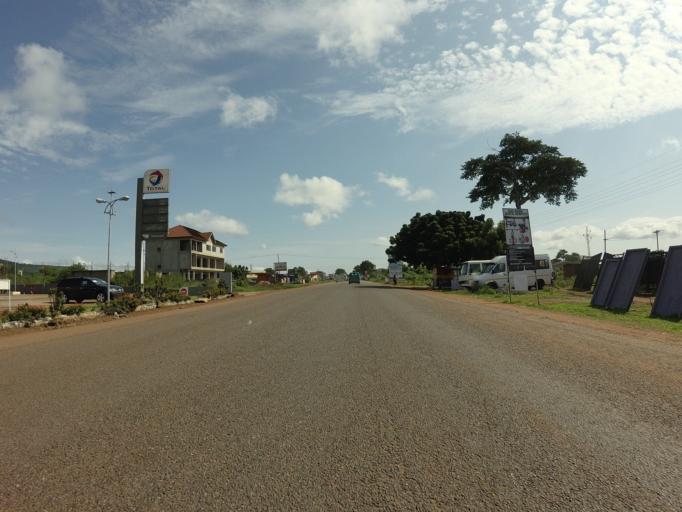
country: GH
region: Eastern
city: Aburi
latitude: 5.7942
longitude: -0.1289
